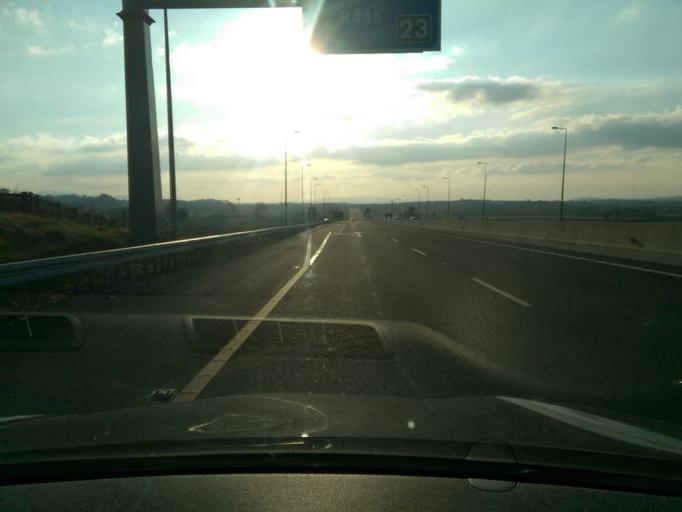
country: IE
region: Munster
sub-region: North Tipperary
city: Templemore
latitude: 52.8867
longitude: -7.9404
